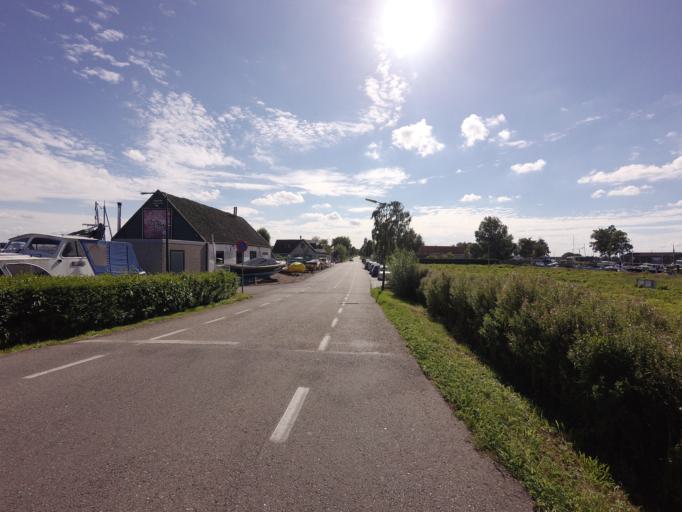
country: NL
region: Utrecht
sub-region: Stichtse Vecht
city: Vreeland
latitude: 52.2350
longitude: 4.9642
